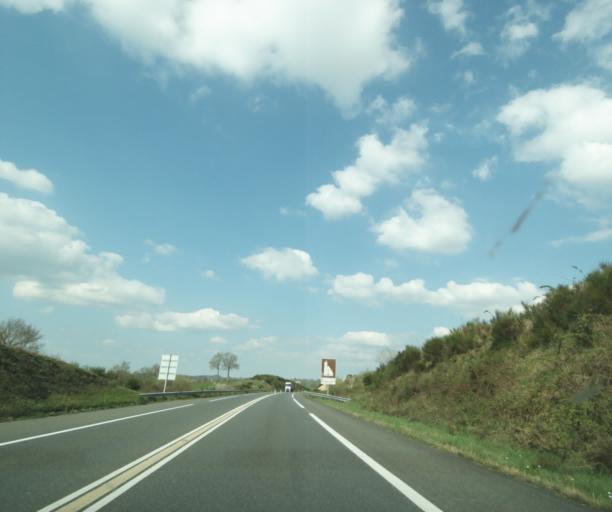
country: FR
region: Auvergne
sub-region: Departement de l'Allier
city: Buxieres-les-Mines
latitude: 46.3923
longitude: 3.0343
